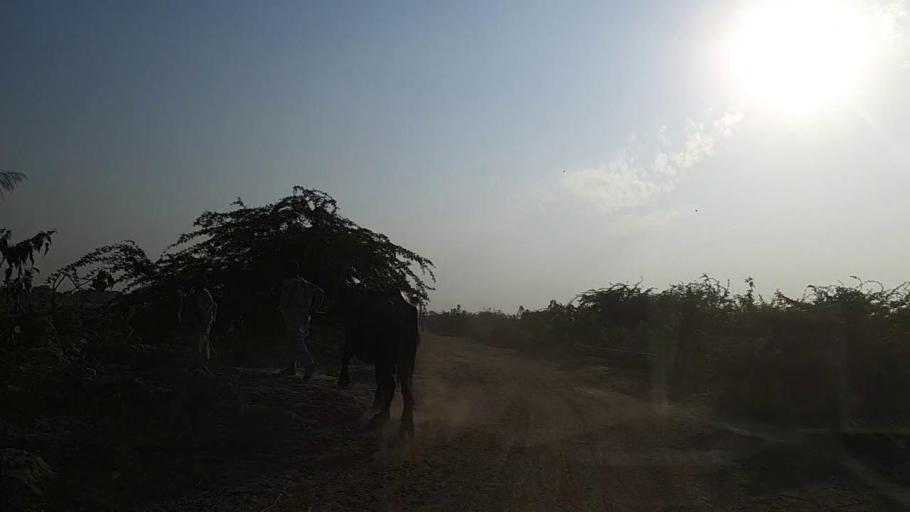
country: PK
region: Sindh
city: Mirpur Batoro
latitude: 24.7710
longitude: 68.2352
